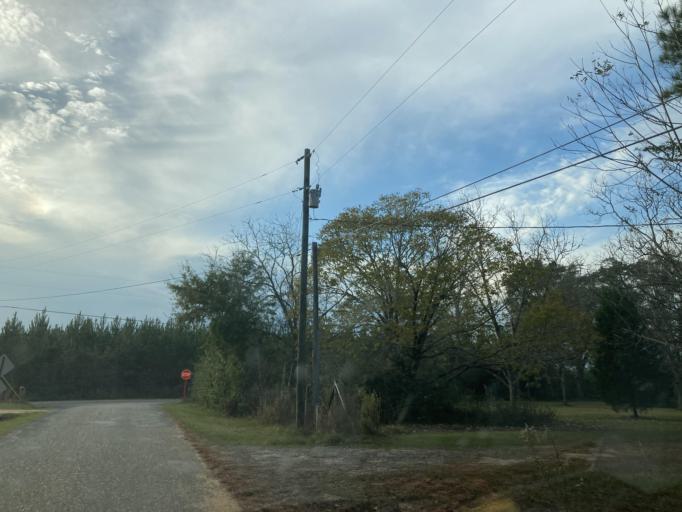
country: US
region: Mississippi
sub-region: Lamar County
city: Purvis
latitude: 31.1959
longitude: -89.3633
